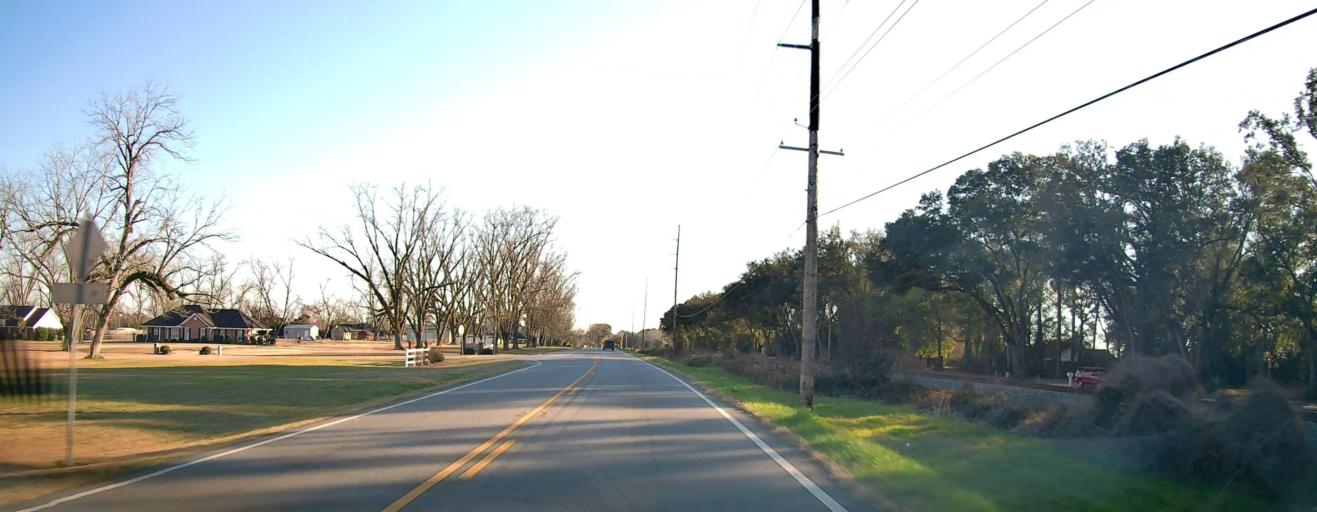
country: US
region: Georgia
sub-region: Dougherty County
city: Albany
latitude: 31.6313
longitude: -84.1632
